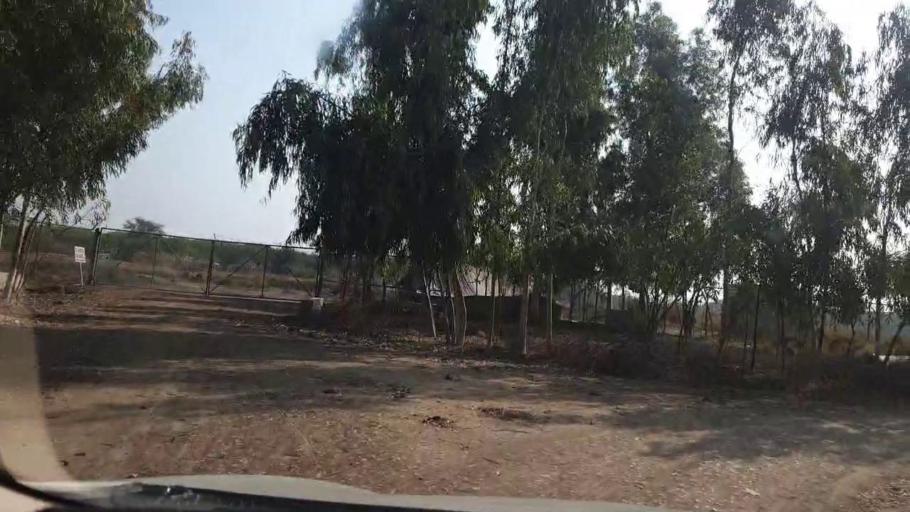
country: PK
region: Sindh
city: Matiari
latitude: 25.6251
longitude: 68.4971
